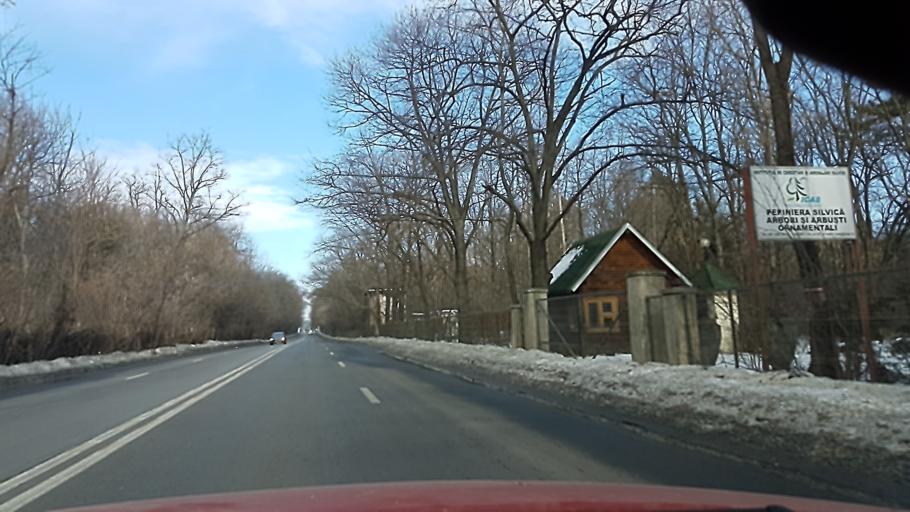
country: RO
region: Ilfov
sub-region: Voluntari City
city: Voluntari
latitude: 44.5041
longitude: 26.1827
